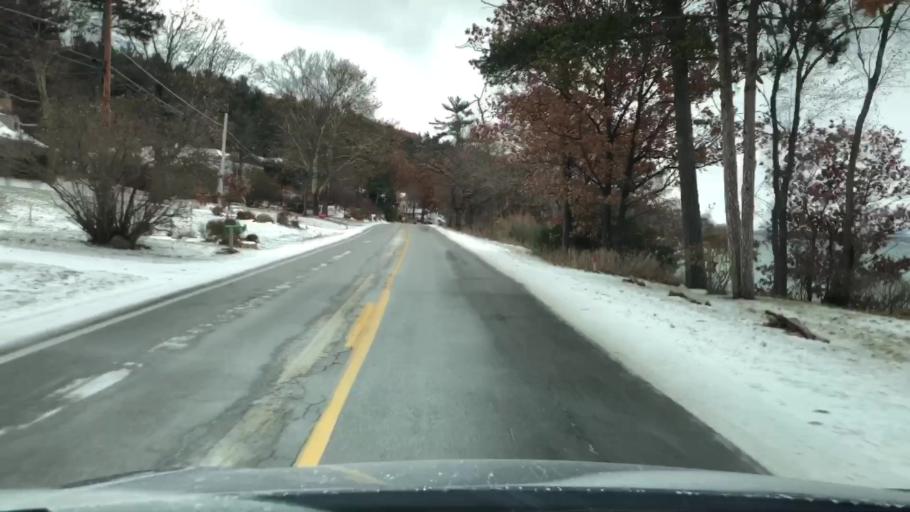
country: US
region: Michigan
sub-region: Grand Traverse County
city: Traverse City
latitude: 44.8045
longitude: -85.5813
